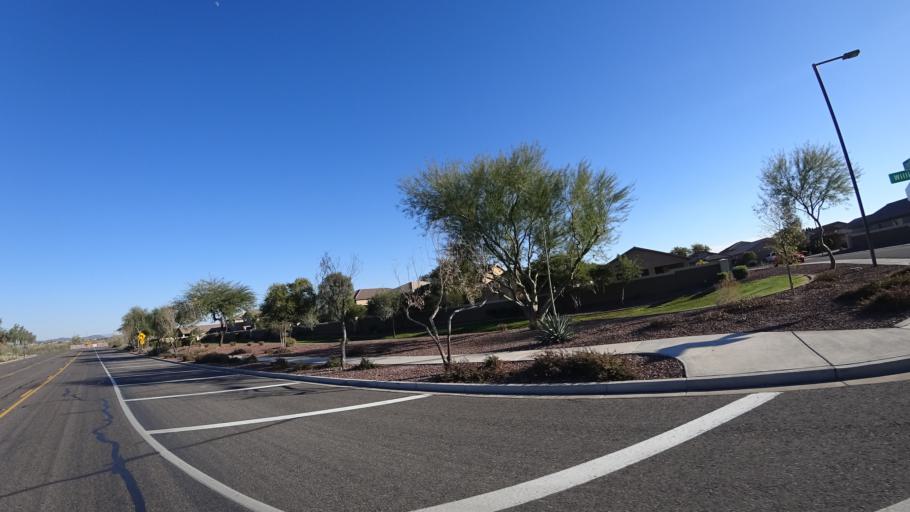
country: US
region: Arizona
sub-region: Maricopa County
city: Sun City West
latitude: 33.6894
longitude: -112.3144
